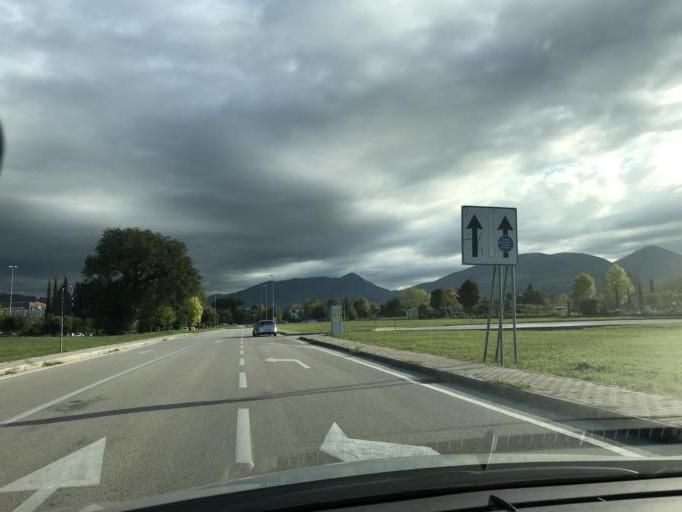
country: IT
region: Umbria
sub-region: Provincia di Perugia
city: Foligno
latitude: 42.9569
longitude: 12.6871
